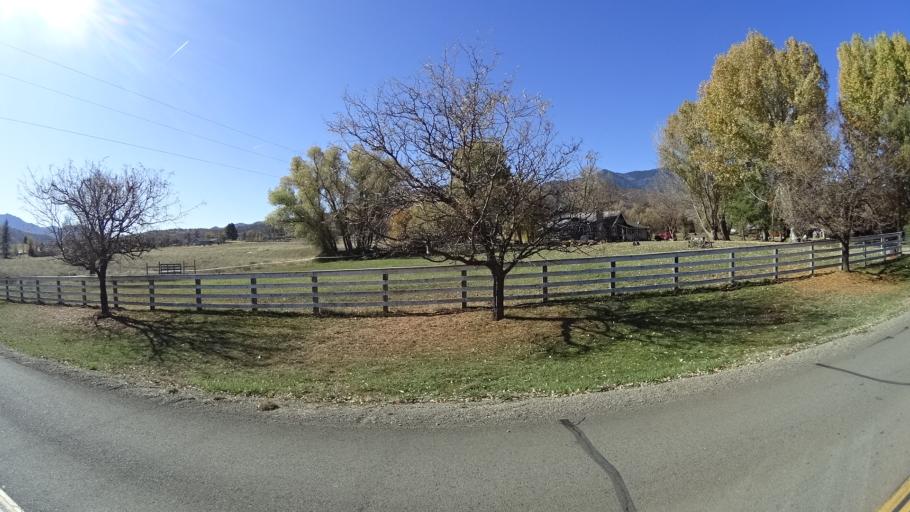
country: US
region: California
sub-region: Siskiyou County
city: Montague
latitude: 41.9016
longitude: -122.5525
